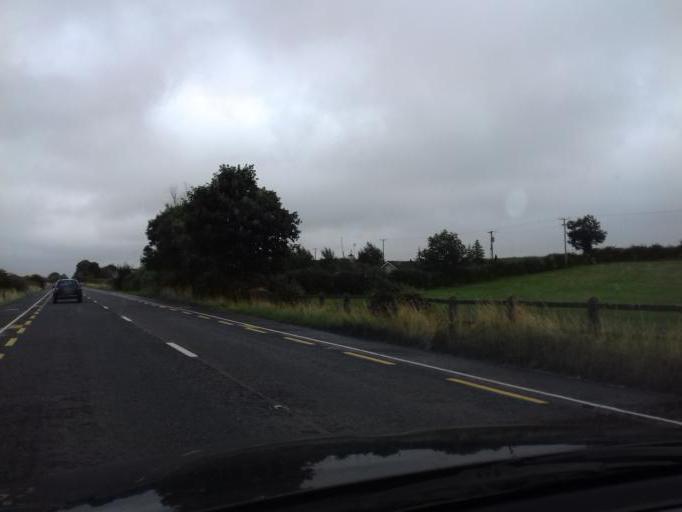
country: IE
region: Leinster
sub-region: County Carlow
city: Bagenalstown
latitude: 52.7498
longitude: -6.9650
